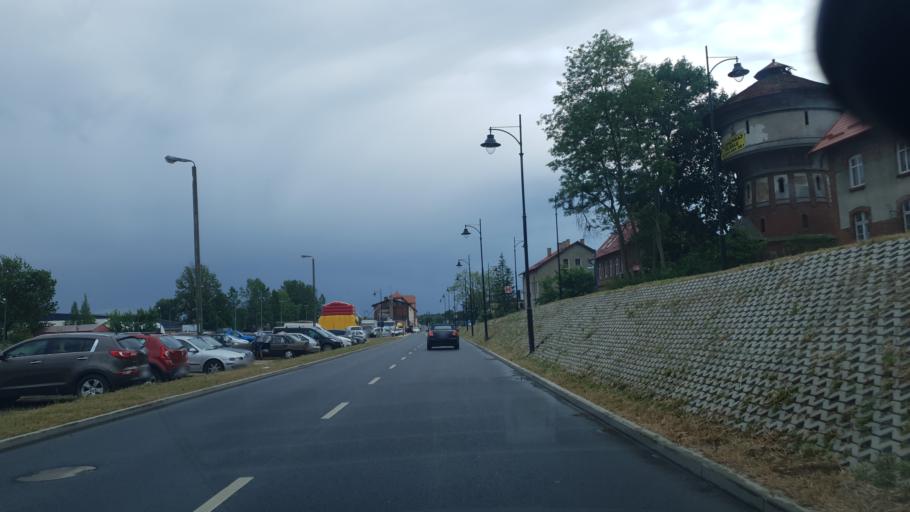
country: PL
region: Pomeranian Voivodeship
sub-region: Powiat kartuski
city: Kartuzy
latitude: 54.3364
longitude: 18.2069
